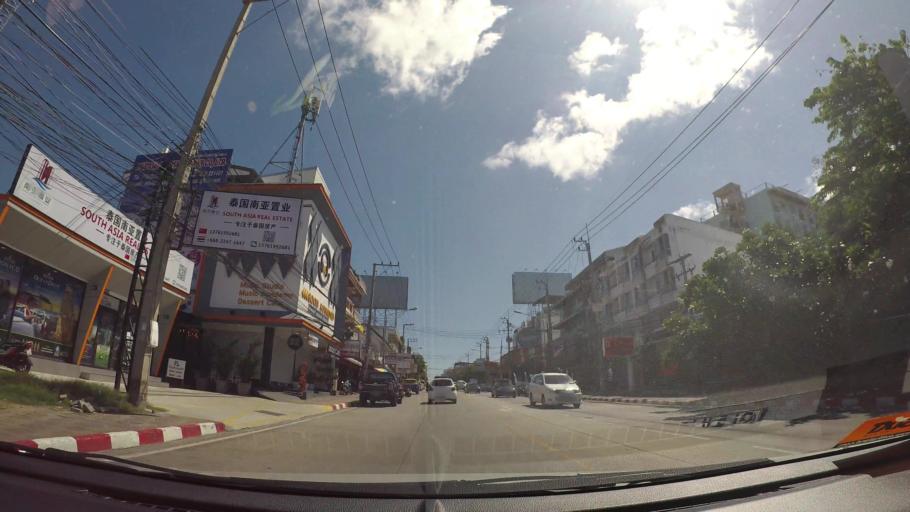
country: TH
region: Chon Buri
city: Phatthaya
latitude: 12.9430
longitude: 100.8951
